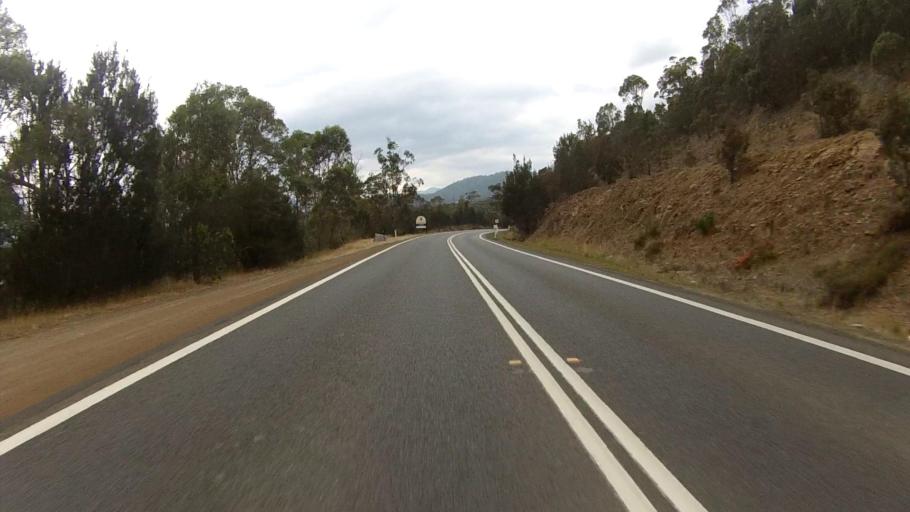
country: AU
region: Tasmania
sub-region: Huon Valley
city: Huonville
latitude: -43.0426
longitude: 147.0528
